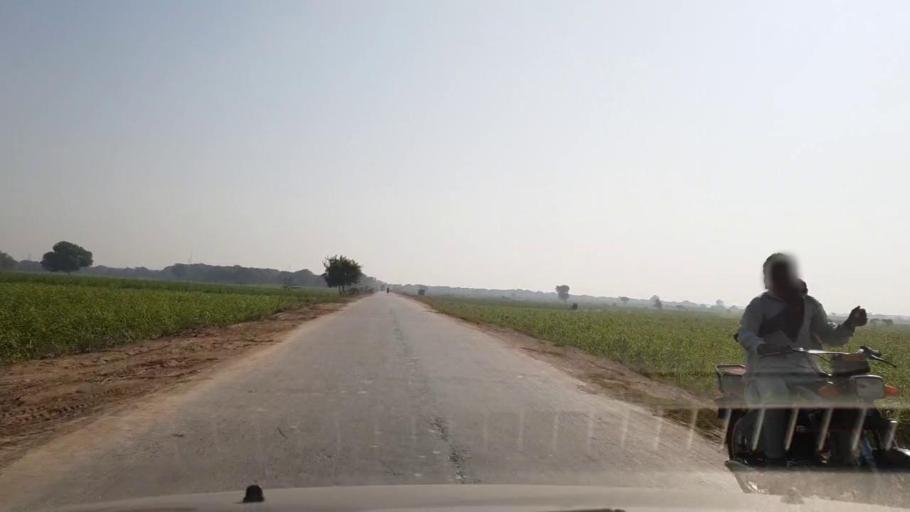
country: PK
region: Sindh
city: Tando Jam
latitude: 25.5202
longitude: 68.6020
